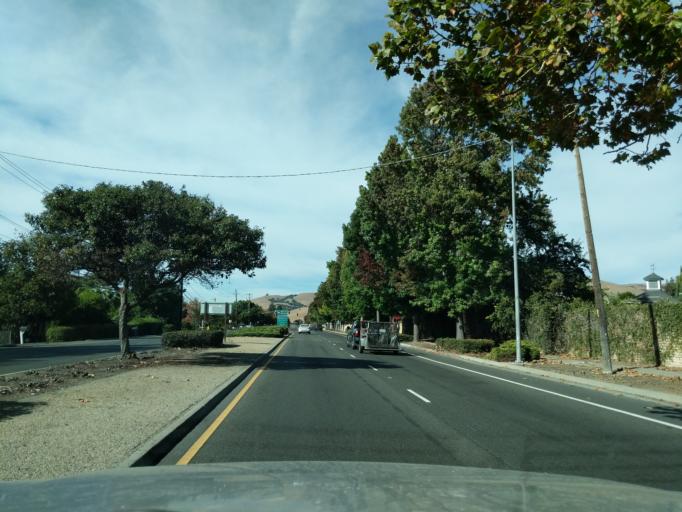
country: US
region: California
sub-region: Alameda County
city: Fremont
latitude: 37.5638
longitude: -121.9599
